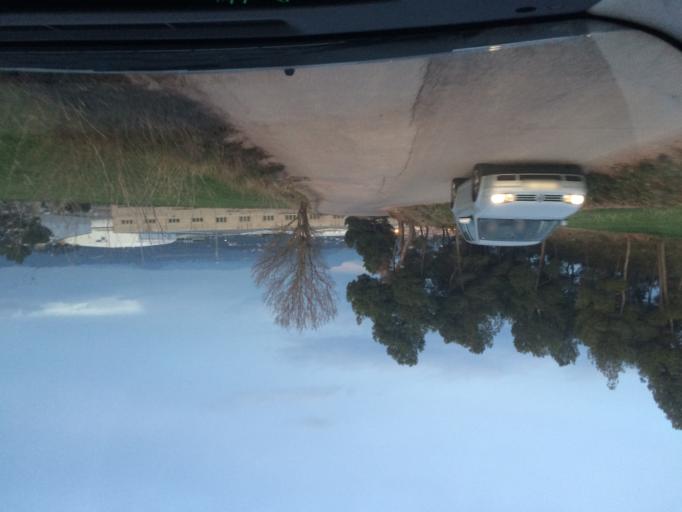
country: ES
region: Catalonia
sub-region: Provincia de Barcelona
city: Sant Fruitos de Bages
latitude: 41.7526
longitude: 1.8586
